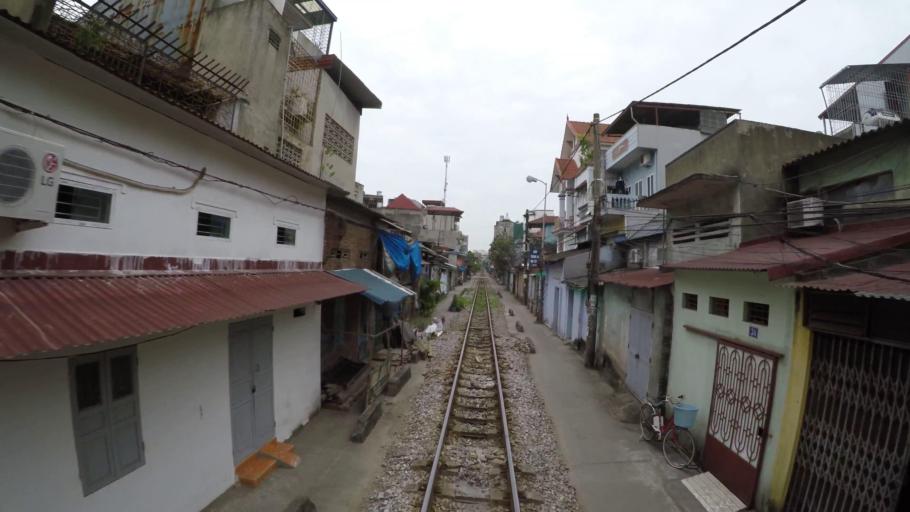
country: VN
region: Hai Phong
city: Haiphong
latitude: 20.8568
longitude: 106.6649
